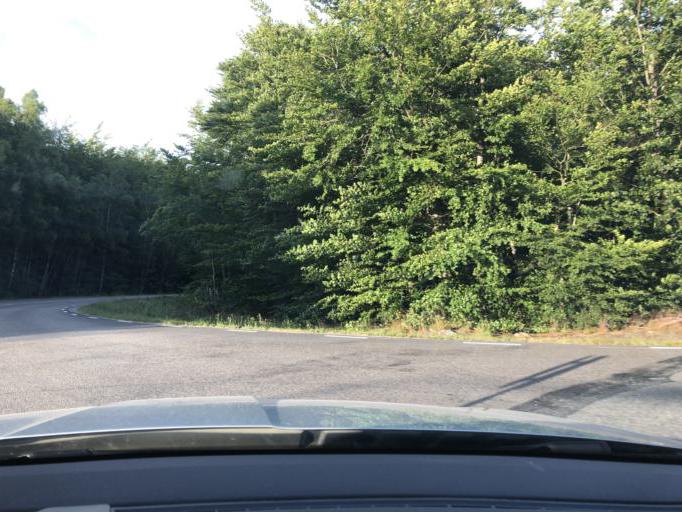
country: SE
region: Blekinge
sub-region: Solvesborgs Kommun
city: Soelvesborg
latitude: 56.0664
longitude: 14.6007
